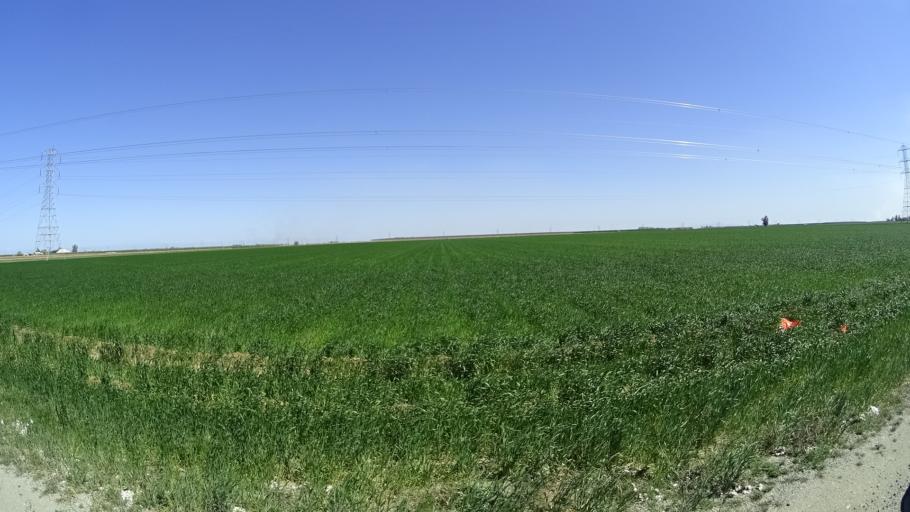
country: US
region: California
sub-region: Glenn County
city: Willows
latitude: 39.4777
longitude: -122.2866
